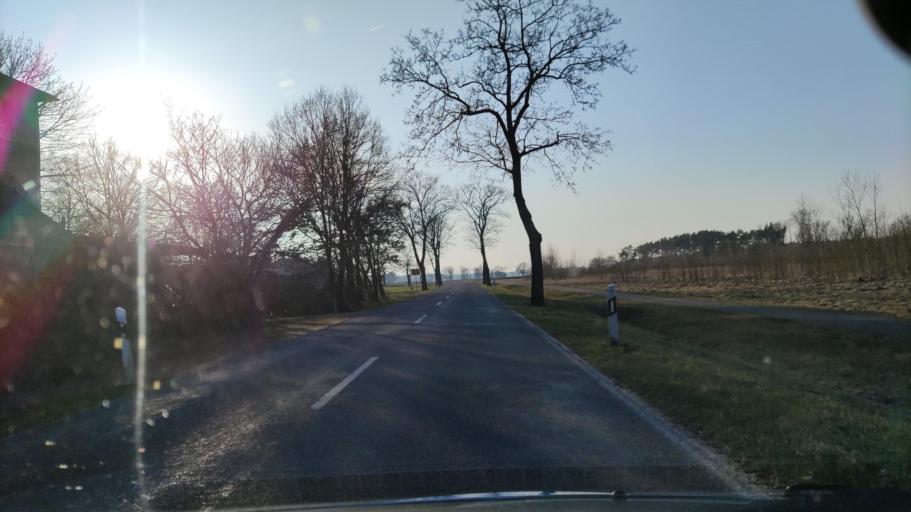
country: DE
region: Brandenburg
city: Lanz
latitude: 52.9932
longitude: 11.5733
